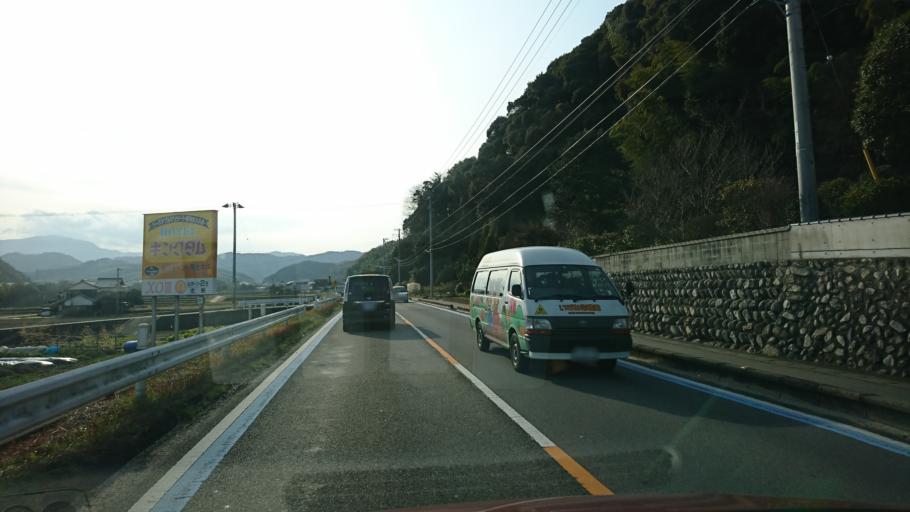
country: JP
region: Ehime
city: Hojo
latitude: 34.0273
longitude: 132.9513
